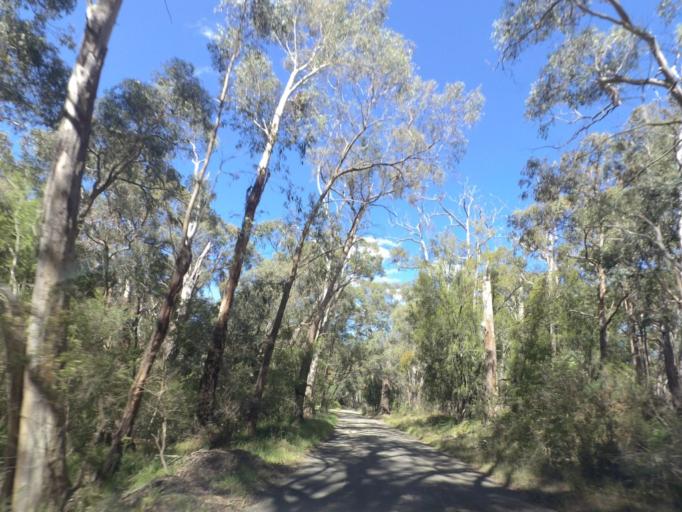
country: AU
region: Victoria
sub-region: Hume
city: Sunbury
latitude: -37.4313
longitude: 144.6537
